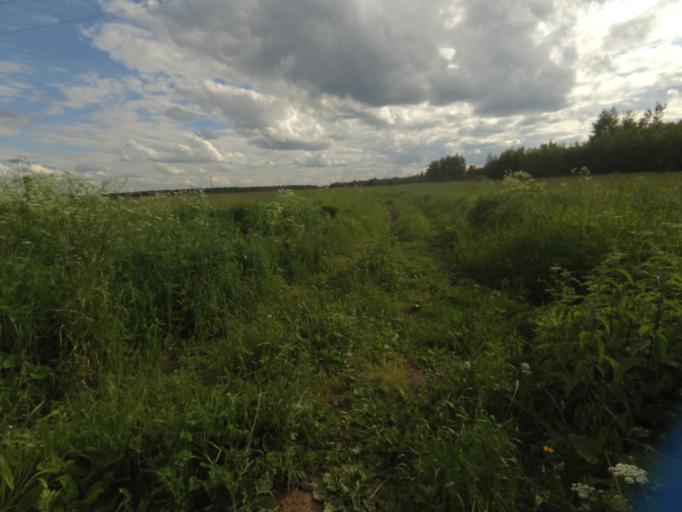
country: RU
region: Moskovskaya
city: Nekrasovskiy
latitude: 56.1100
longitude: 37.5179
